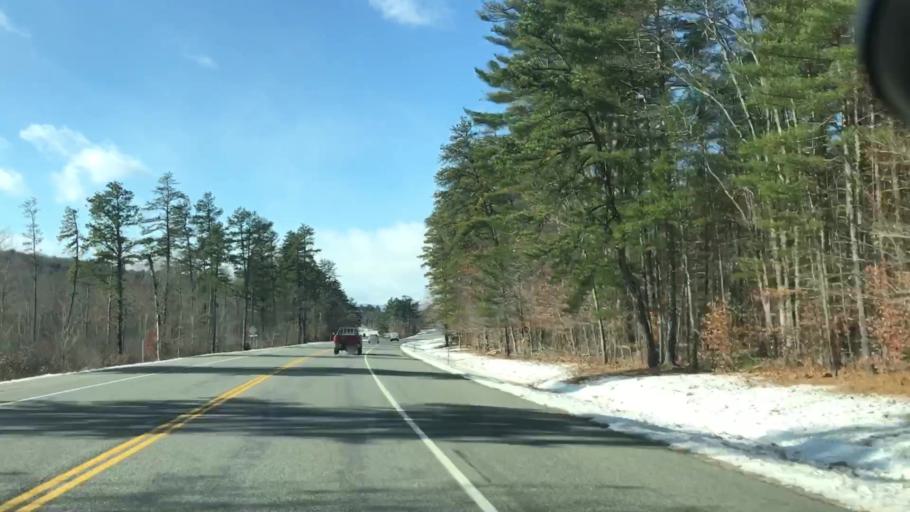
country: US
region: New Hampshire
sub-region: Carroll County
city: Freedom
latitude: 43.7926
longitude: -71.0248
